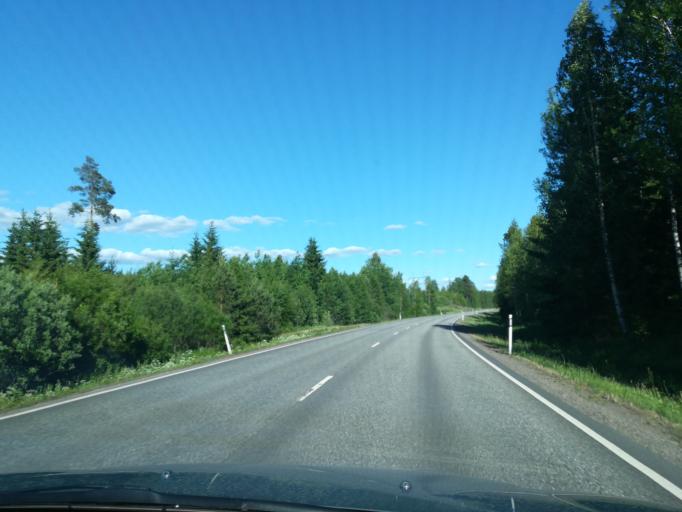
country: FI
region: South Karelia
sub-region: Imatra
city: Ruokolahti
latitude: 61.3507
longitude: 28.7476
